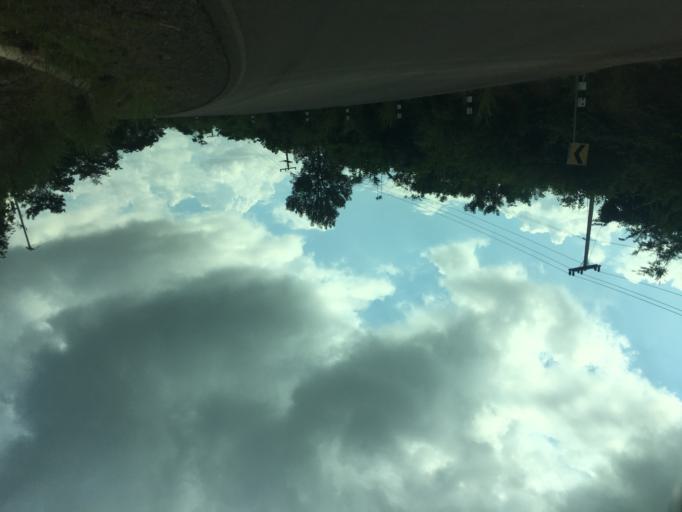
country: TH
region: Nong Khai
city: Sangkhom
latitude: 18.1887
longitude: 102.2087
